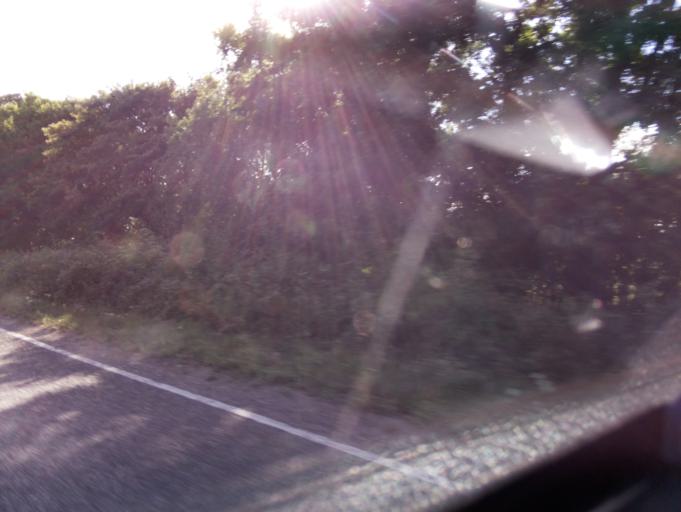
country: GB
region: England
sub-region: Hampshire
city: Romsey
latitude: 50.9758
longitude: -1.5178
